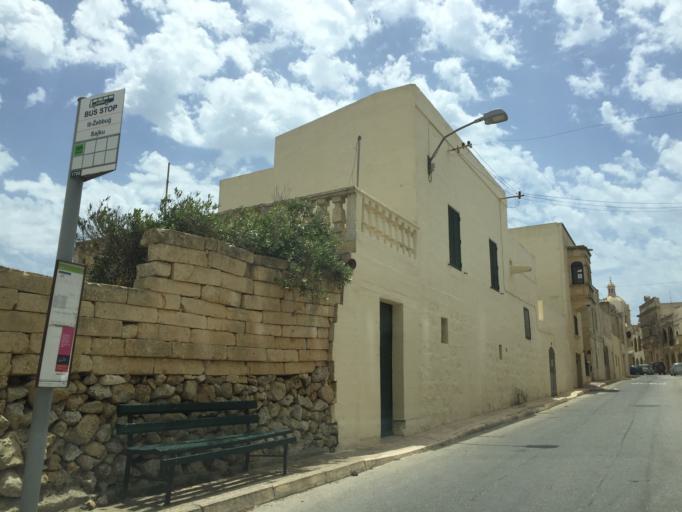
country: MT
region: Iz-Zebbug
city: Zebbug
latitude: 36.0719
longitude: 14.2371
